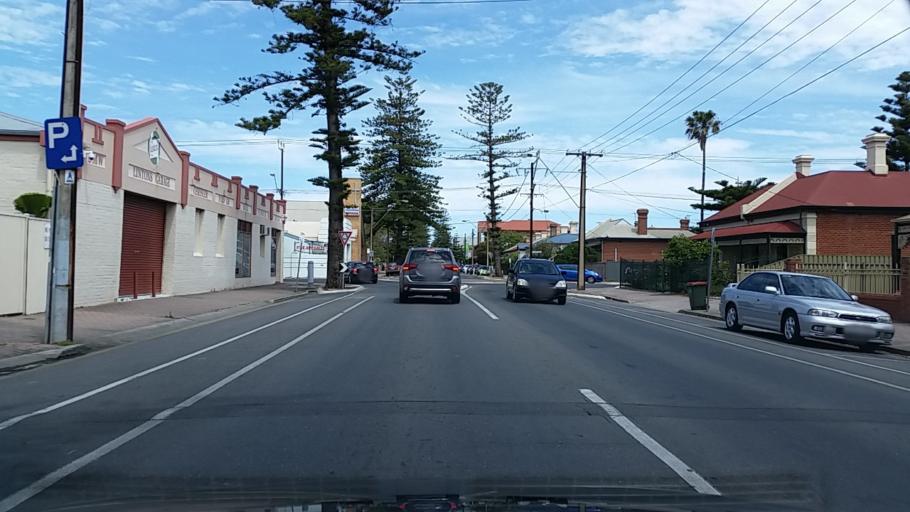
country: AU
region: South Australia
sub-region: Adelaide
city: Glenelg
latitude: -34.9778
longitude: 138.5176
